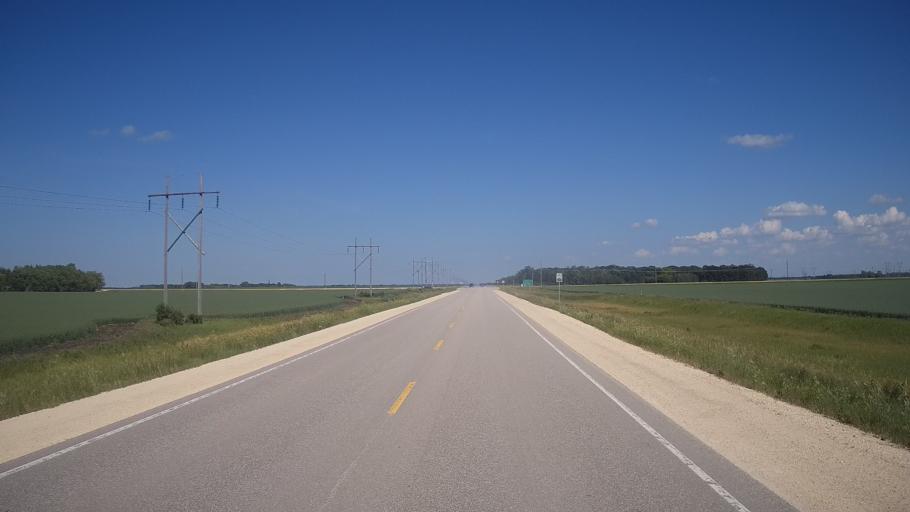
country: CA
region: Manitoba
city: Stonewall
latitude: 50.1227
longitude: -97.4430
